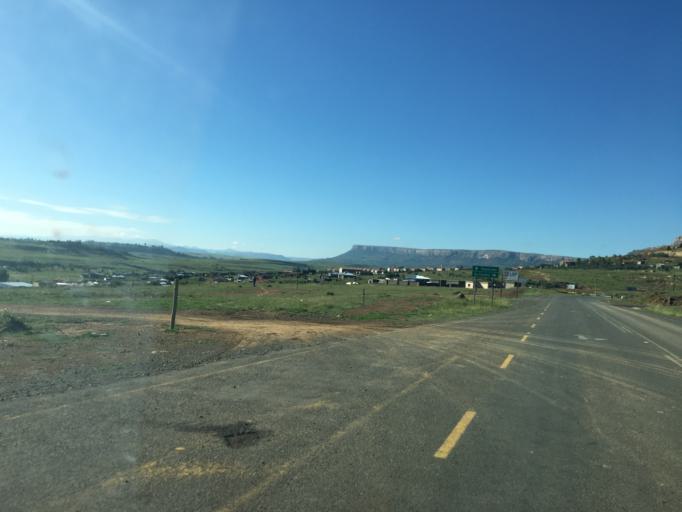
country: LS
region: Maseru
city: Maseru
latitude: -29.3858
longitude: 27.4706
